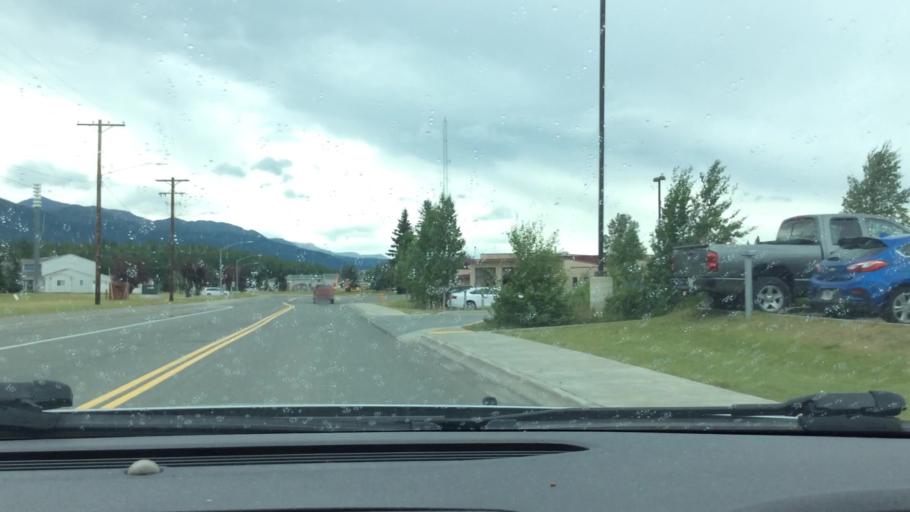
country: US
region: Alaska
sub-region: Anchorage Municipality
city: Elmendorf Air Force Base
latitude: 61.2555
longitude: -149.6840
